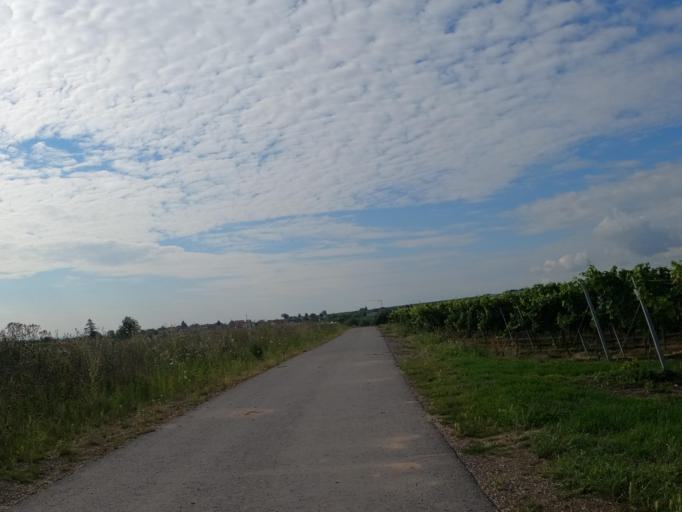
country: DE
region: Rheinland-Pfalz
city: Kirchheim an der Weinstrasse
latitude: 49.5300
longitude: 8.1765
